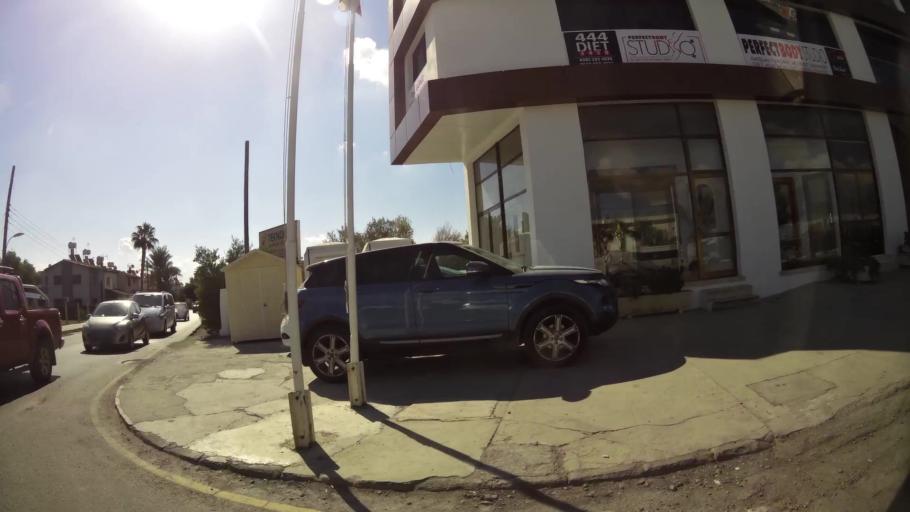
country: CY
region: Lefkosia
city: Nicosia
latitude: 35.2118
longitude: 33.3358
